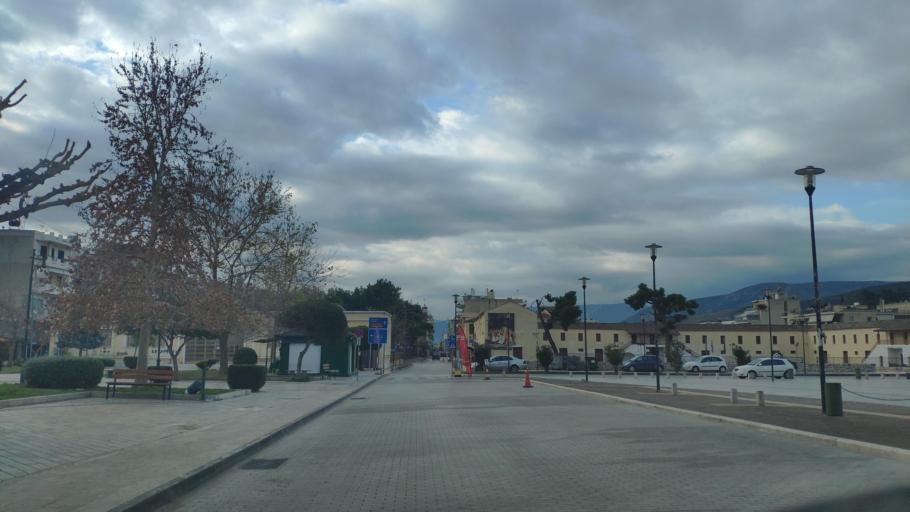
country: GR
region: Peloponnese
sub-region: Nomos Argolidos
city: Argos
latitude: 37.6353
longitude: 22.7264
